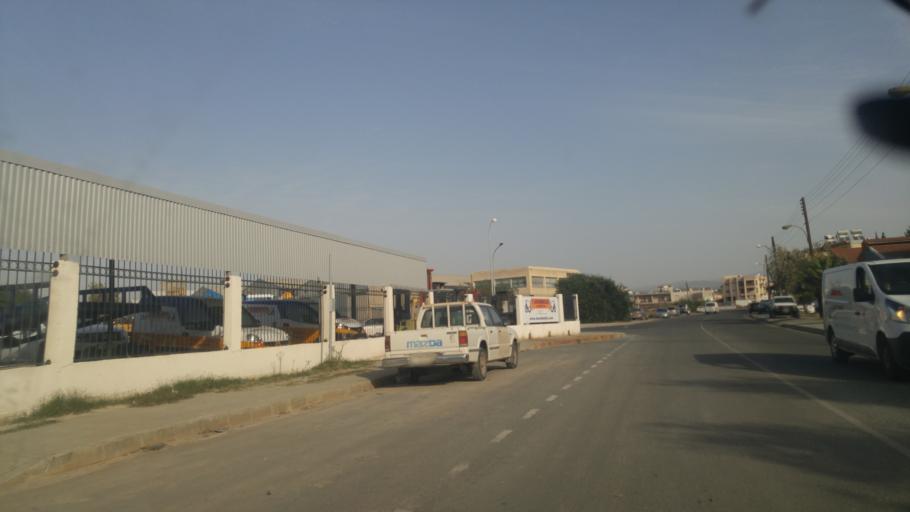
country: CY
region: Limassol
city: Pano Polemidia
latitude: 34.6727
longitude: 32.9935
